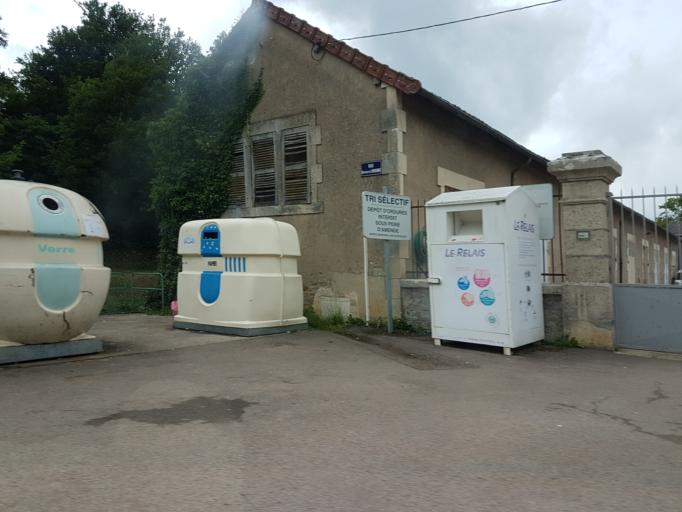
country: FR
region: Bourgogne
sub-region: Departement de la Nievre
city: Corbigny
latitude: 47.2591
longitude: 3.6801
